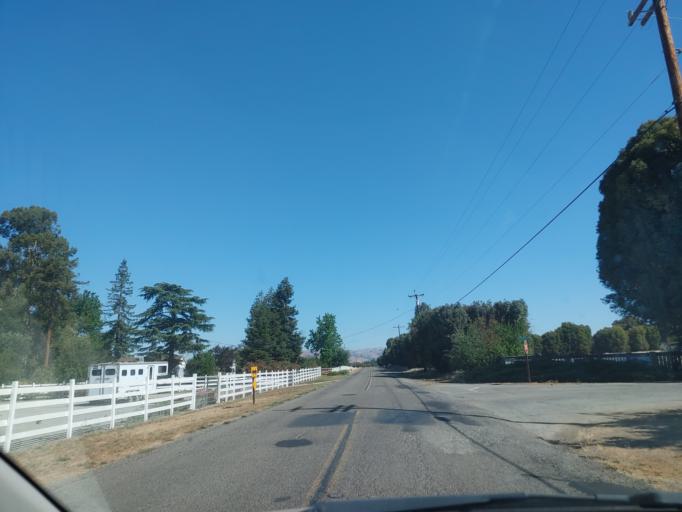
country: US
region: California
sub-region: San Benito County
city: Hollister
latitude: 36.9078
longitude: -121.3516
